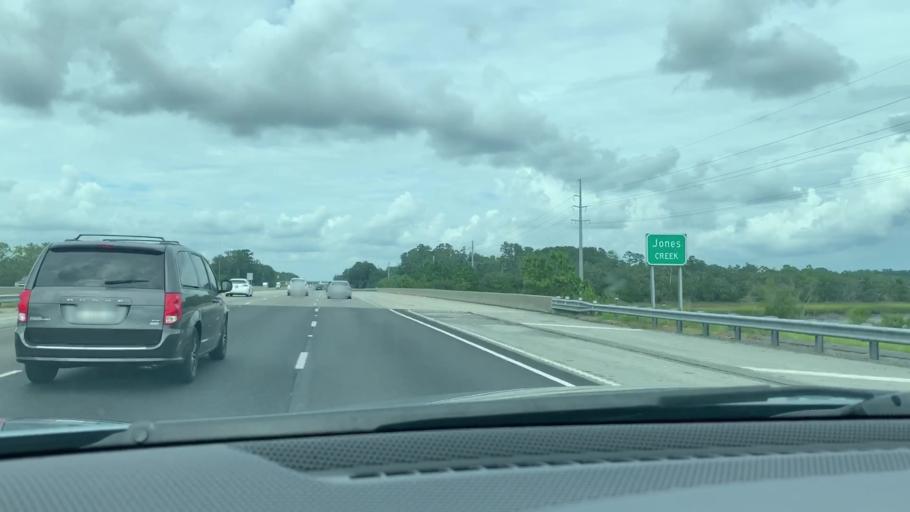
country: US
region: Georgia
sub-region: Liberty County
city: Midway
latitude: 31.8061
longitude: -81.3674
